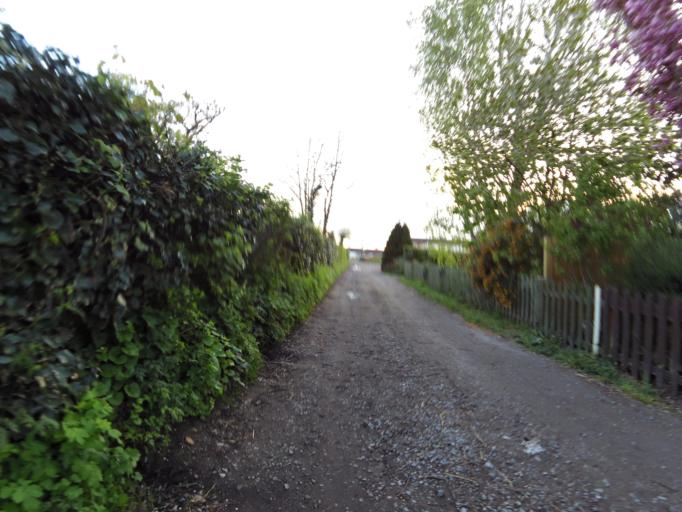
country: GB
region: England
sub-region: Suffolk
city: Kesgrave
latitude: 52.0725
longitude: 1.1981
